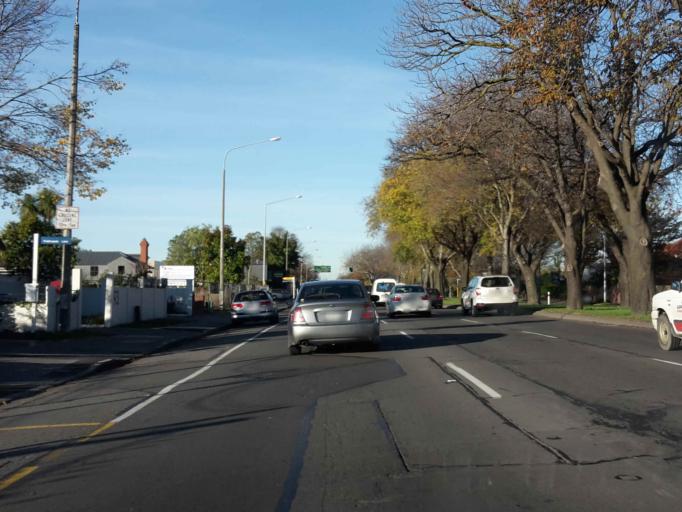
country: NZ
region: Canterbury
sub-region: Christchurch City
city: Christchurch
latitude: -43.5208
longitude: 172.6311
